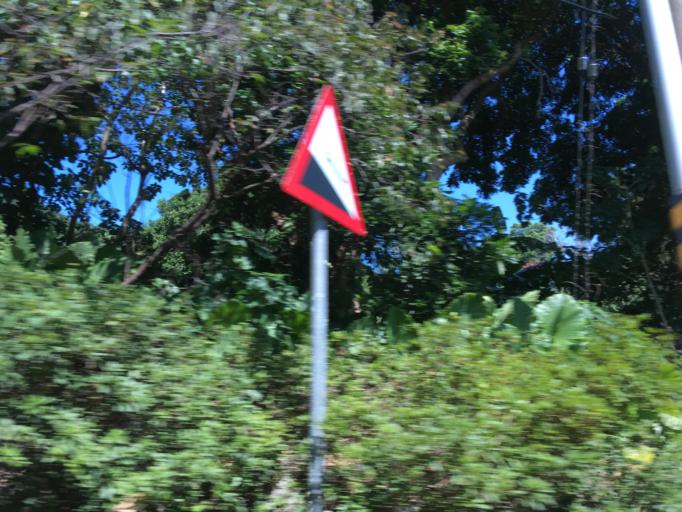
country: TW
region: Taipei
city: Taipei
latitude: 25.1493
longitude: 121.5051
